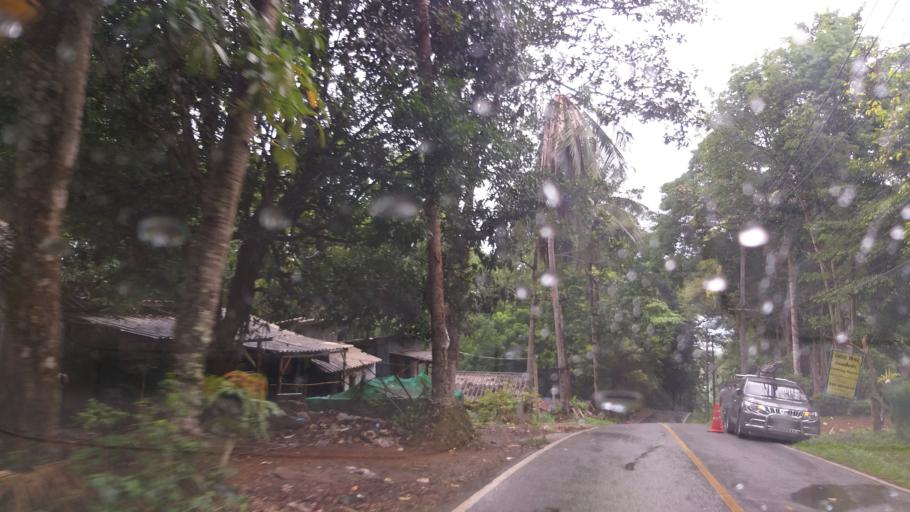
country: TH
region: Trat
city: Ko Chang Tai
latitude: 11.9853
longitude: 102.2999
